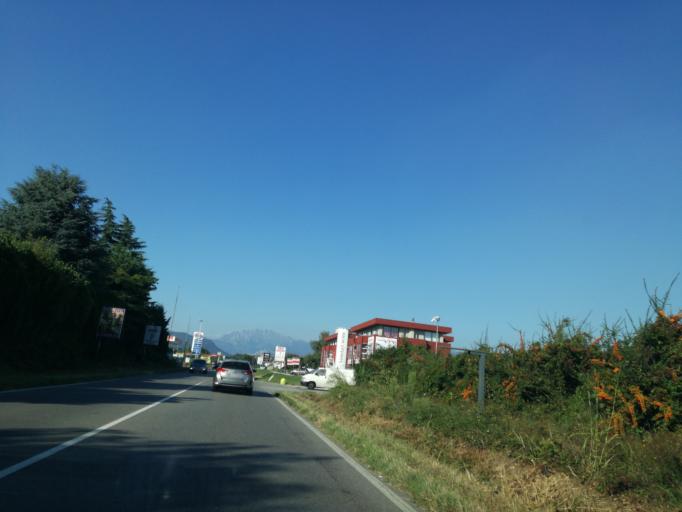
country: IT
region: Lombardy
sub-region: Provincia di Lecco
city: Cernusco Lombardone
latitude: 45.6822
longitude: 9.3980
